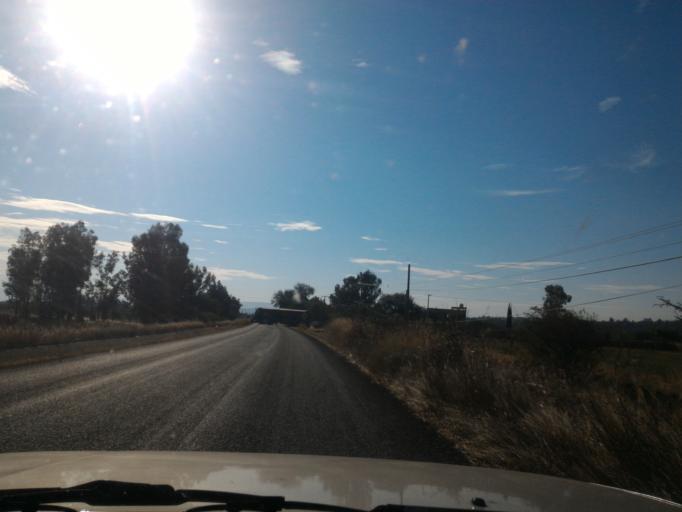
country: MX
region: Guanajuato
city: Ciudad Manuel Doblado
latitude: 20.7475
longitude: -101.9605
